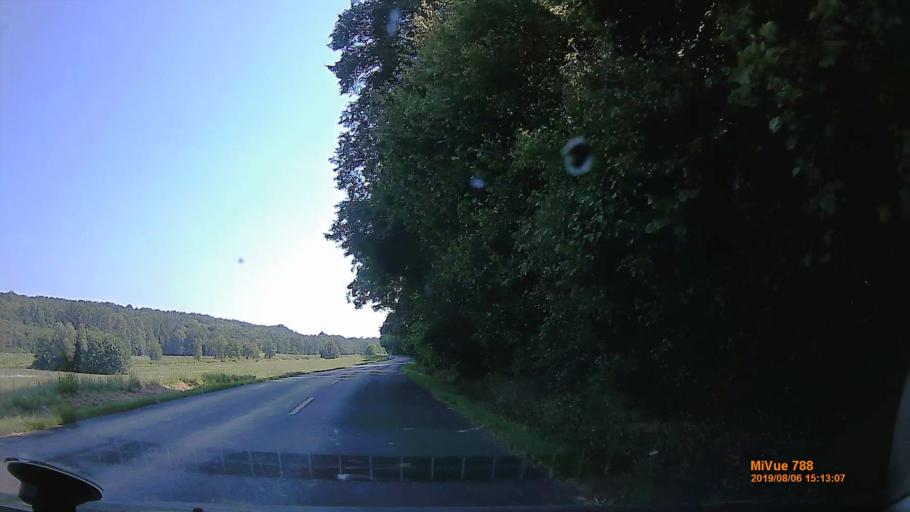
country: HU
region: Zala
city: Murakeresztur
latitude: 46.3585
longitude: 16.9773
